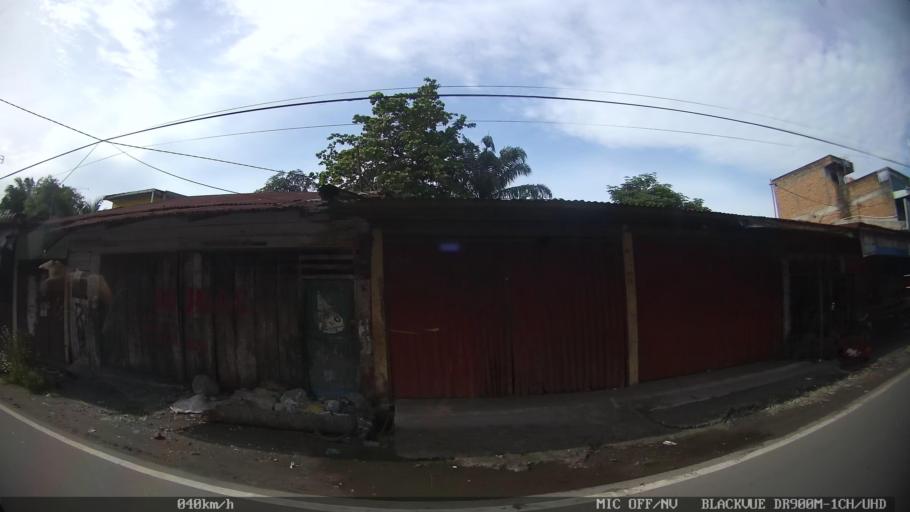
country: ID
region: North Sumatra
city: Sunggal
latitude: 3.6104
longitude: 98.6344
